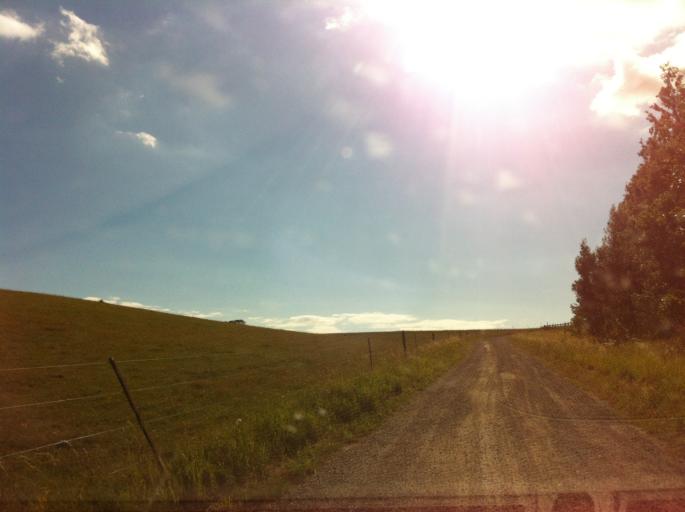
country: SE
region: Skane
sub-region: Ystads Kommun
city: Kopingebro
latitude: 55.3922
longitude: 14.0470
